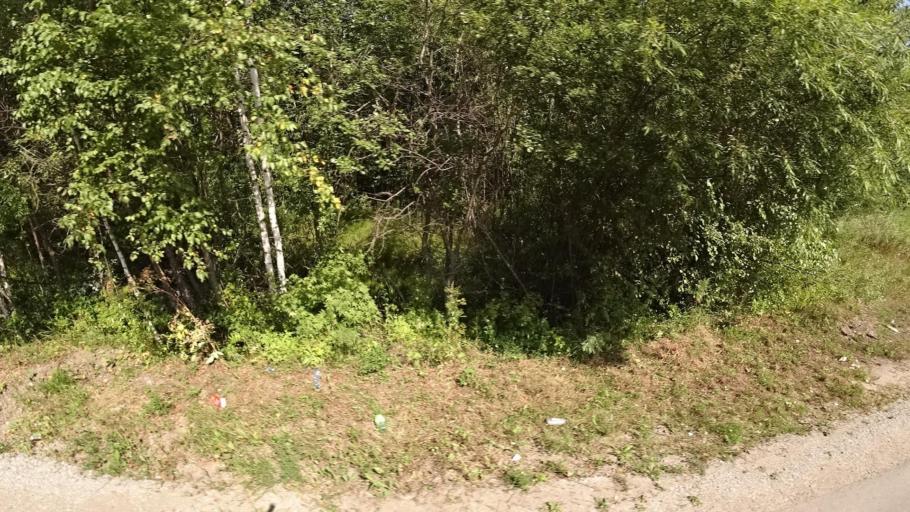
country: RU
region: Khabarovsk Krai
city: Khor
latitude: 47.9724
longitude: 135.1152
